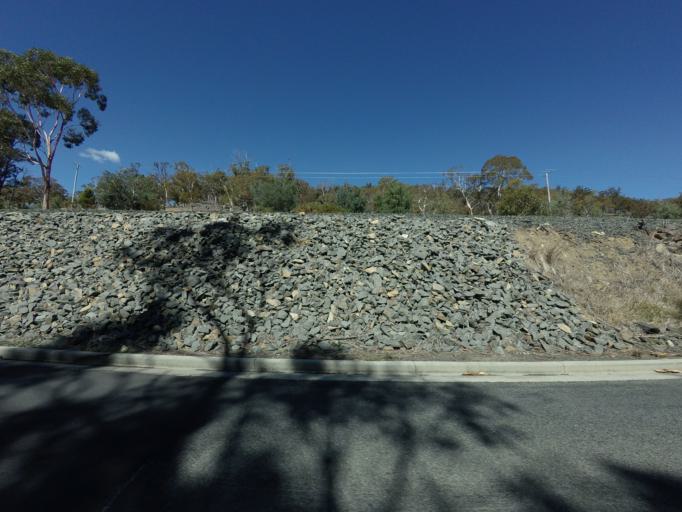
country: AU
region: Tasmania
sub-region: Northern Midlands
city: Evandale
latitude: -41.7368
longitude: 147.8074
